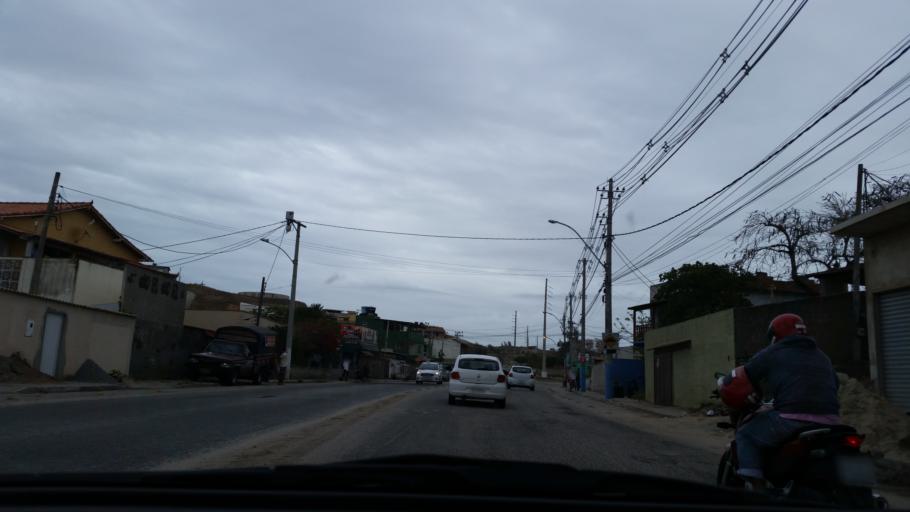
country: BR
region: Rio de Janeiro
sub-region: Cabo Frio
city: Cabo Frio
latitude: -22.8555
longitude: -42.0458
